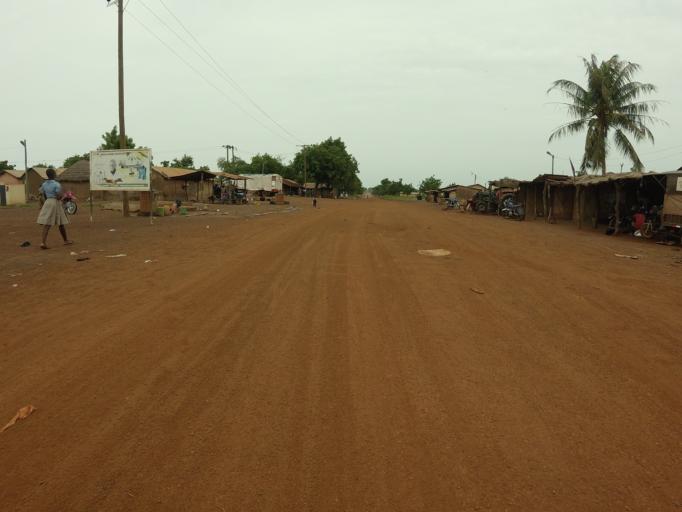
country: GH
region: Northern
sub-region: Yendi
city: Yendi
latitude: 9.0556
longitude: -0.0121
